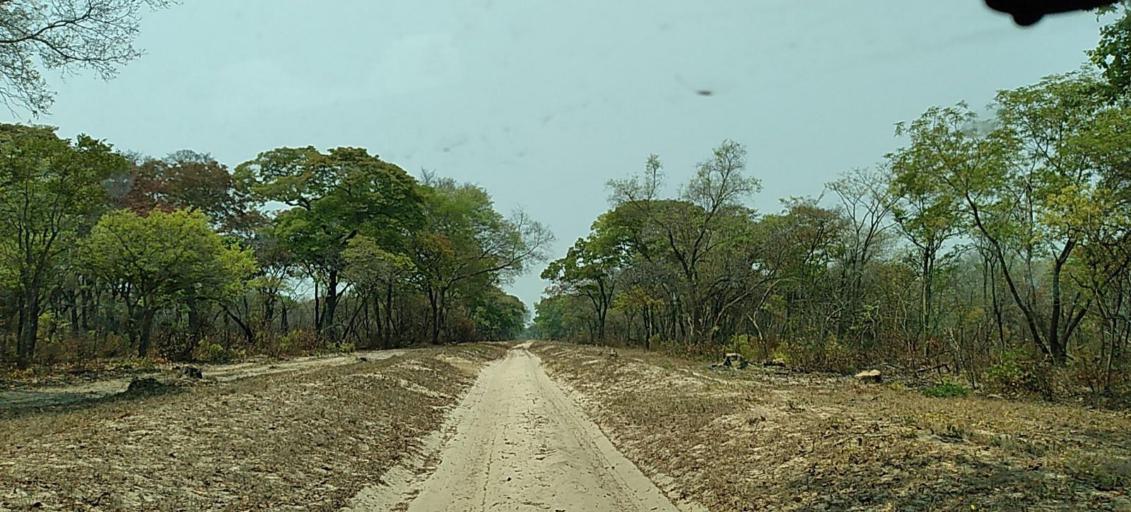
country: ZM
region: Western
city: Lukulu
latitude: -14.1367
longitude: 23.2768
